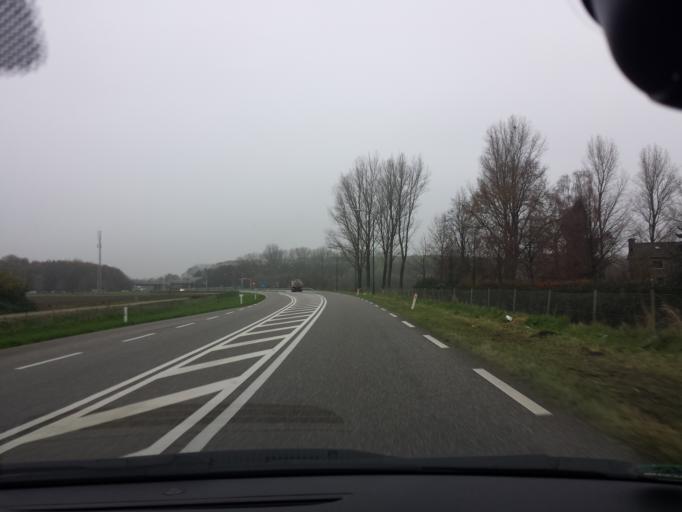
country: NL
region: North Brabant
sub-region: Gemeente Landerd
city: Reek
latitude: 51.7865
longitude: 5.6629
